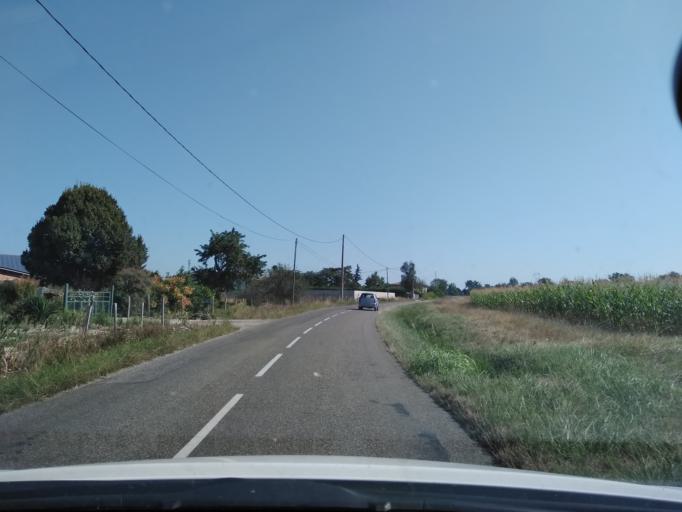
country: FR
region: Midi-Pyrenees
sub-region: Departement du Tarn-et-Garonne
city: Montech
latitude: 43.9758
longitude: 1.2450
